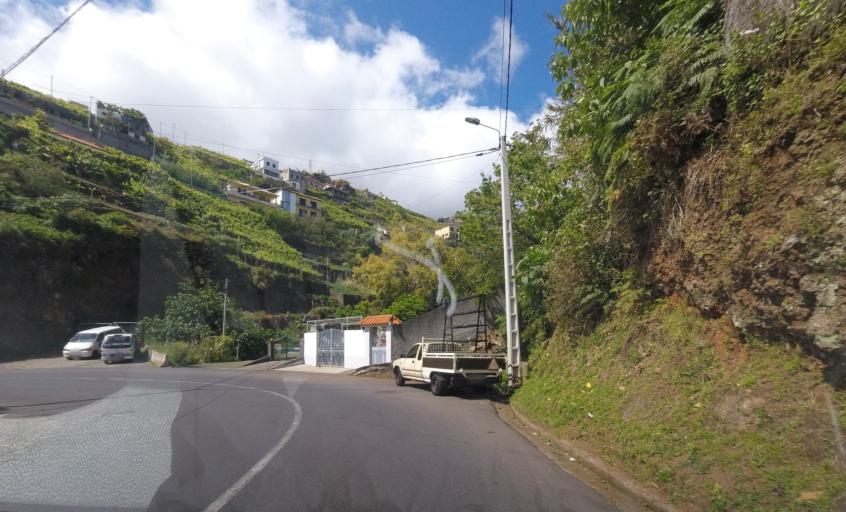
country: PT
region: Madeira
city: Camara de Lobos
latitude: 32.6750
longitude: -16.9759
